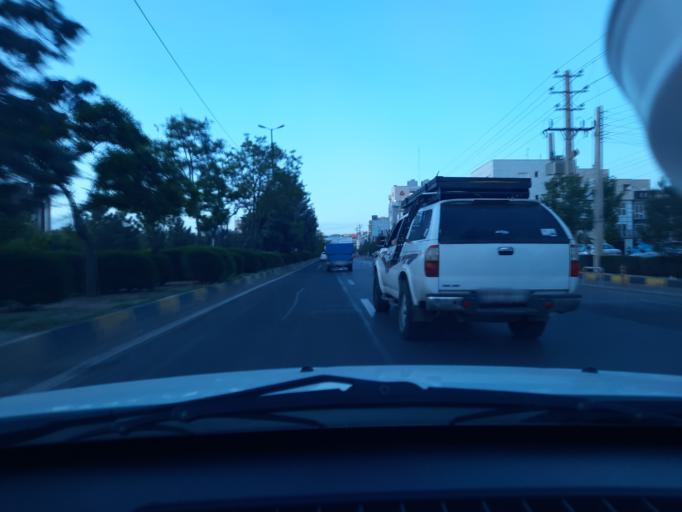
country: IR
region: Qazvin
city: Qazvin
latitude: 36.3062
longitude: 50.0118
